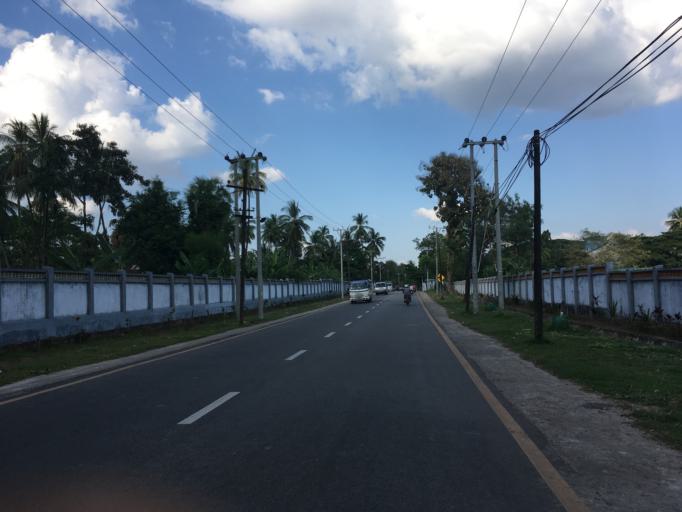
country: MM
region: Mon
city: Mawlamyine
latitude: 16.4427
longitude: 97.6180
